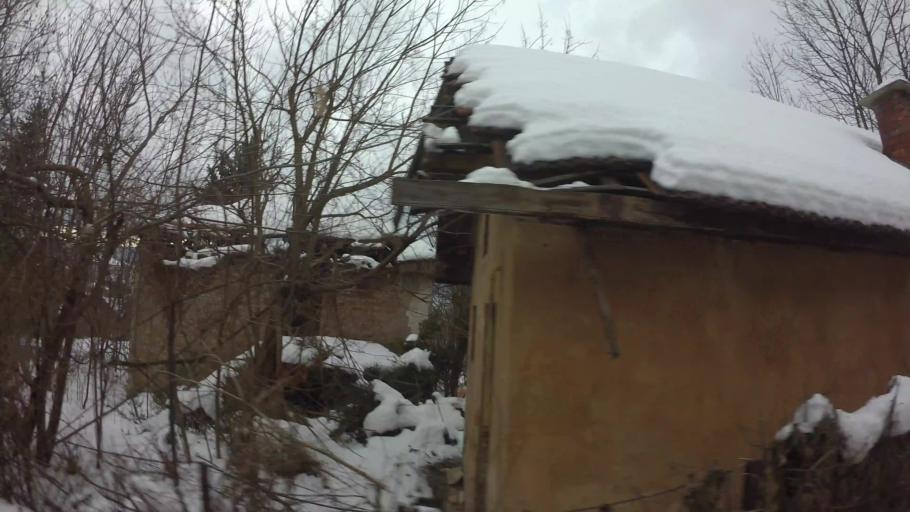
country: BA
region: Federation of Bosnia and Herzegovina
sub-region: Kanton Sarajevo
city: Sarajevo
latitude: 43.8640
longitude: 18.3196
